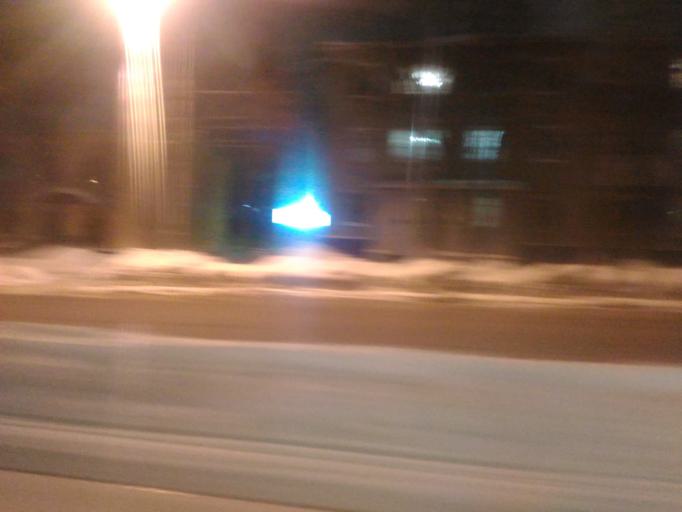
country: RU
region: Ulyanovsk
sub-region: Ulyanovskiy Rayon
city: Ulyanovsk
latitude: 54.3456
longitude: 48.3731
